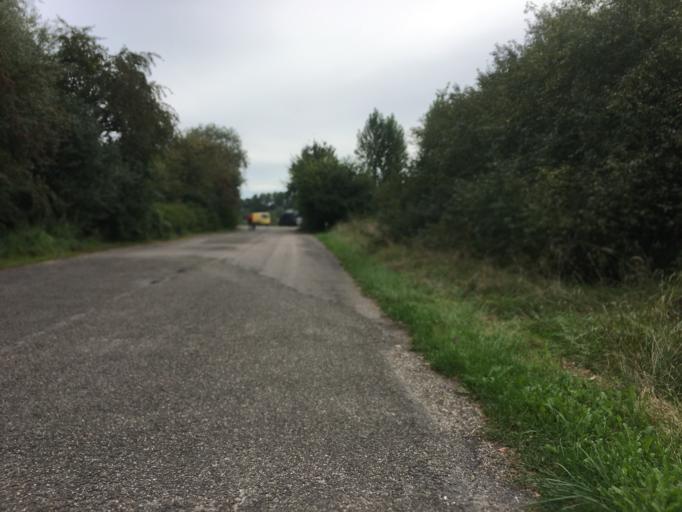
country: DE
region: Baden-Wuerttemberg
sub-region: Karlsruhe Region
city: Bruhl
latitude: 49.3935
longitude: 8.5017
